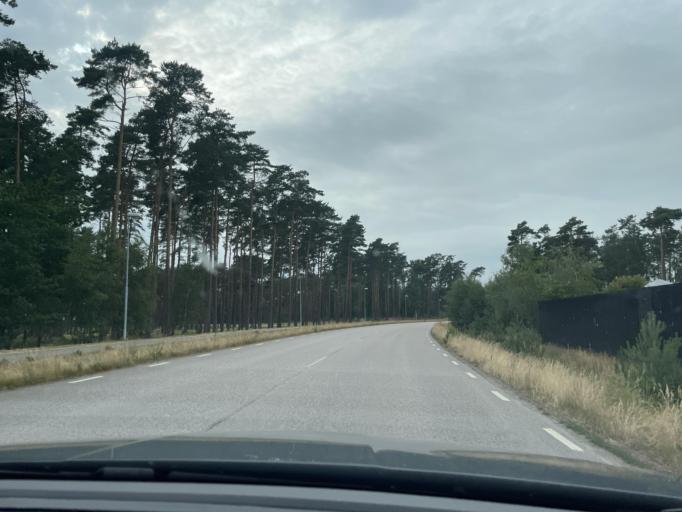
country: SE
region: Blekinge
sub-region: Solvesborgs Kommun
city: Soelvesborg
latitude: 56.0446
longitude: 14.6116
